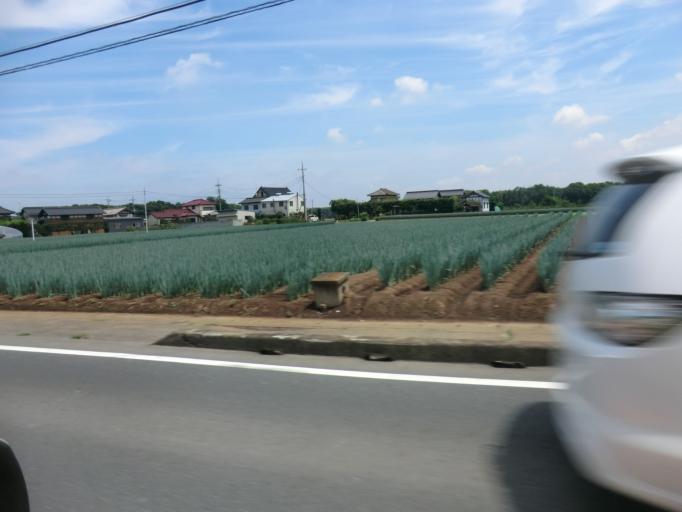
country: JP
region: Ibaraki
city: Iwai
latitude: 36.0748
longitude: 139.8546
